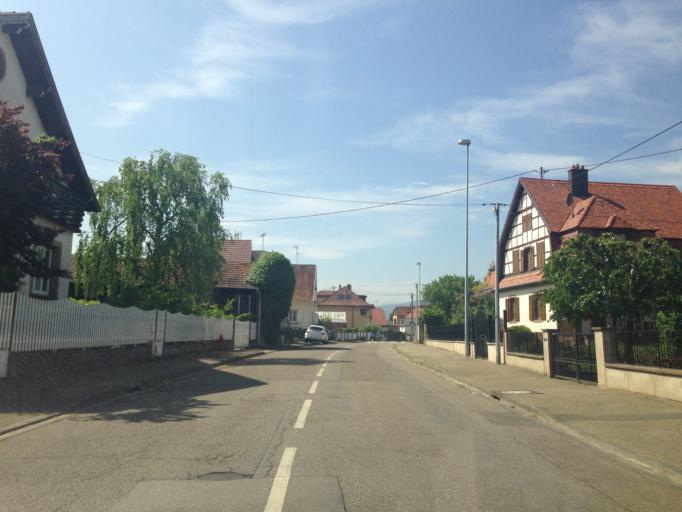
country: FR
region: Alsace
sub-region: Departement du Bas-Rhin
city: Obernai
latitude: 48.4585
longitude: 7.4823
